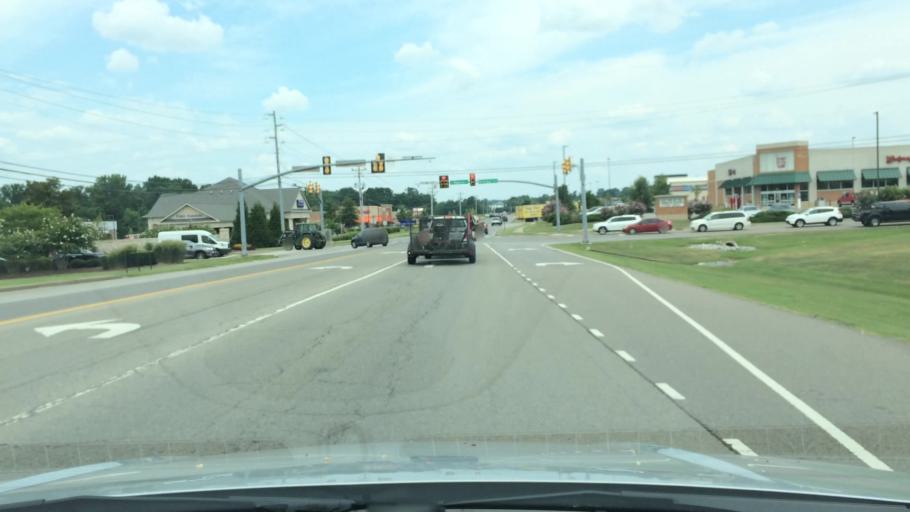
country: US
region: Tennessee
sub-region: Maury County
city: Spring Hill
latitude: 35.7371
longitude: -86.8939
